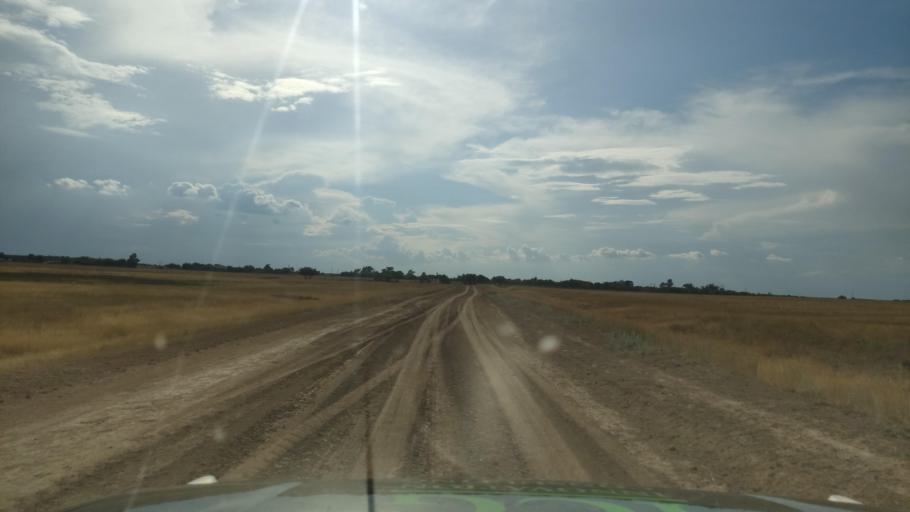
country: KZ
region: Pavlodar
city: Pavlodar
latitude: 52.5154
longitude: 77.4575
